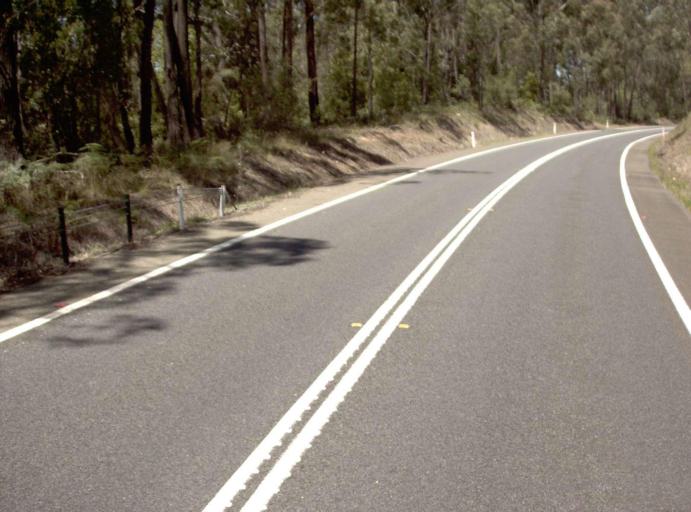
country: AU
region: Victoria
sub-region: East Gippsland
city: Lakes Entrance
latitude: -37.7843
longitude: 148.0542
